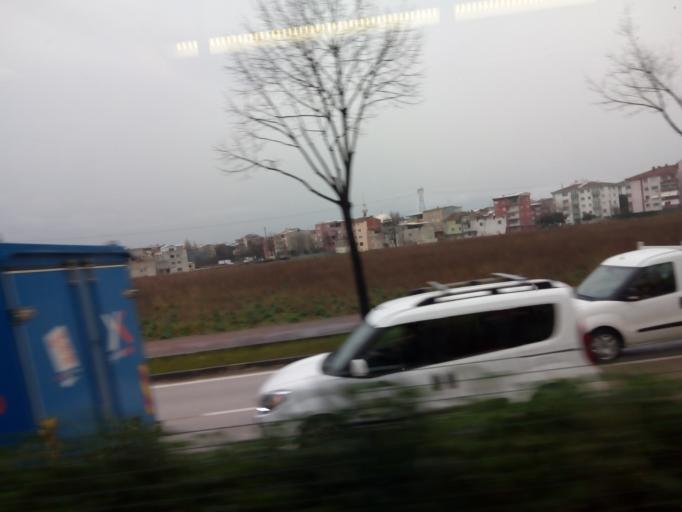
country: TR
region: Bursa
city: Yildirim
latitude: 40.2085
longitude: 29.0266
